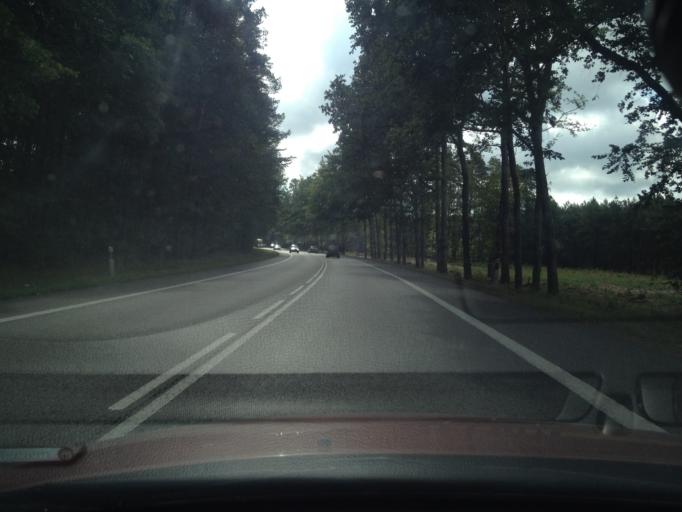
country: PL
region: West Pomeranian Voivodeship
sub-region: Powiat goleniowski
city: Przybiernow
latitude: 53.6871
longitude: 14.7984
